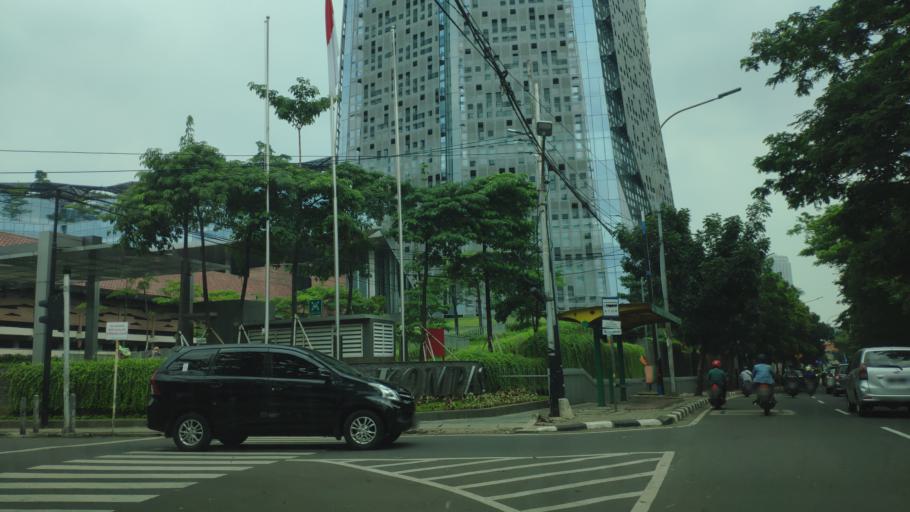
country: ID
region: Jakarta Raya
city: Jakarta
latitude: -6.2106
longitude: 106.7960
